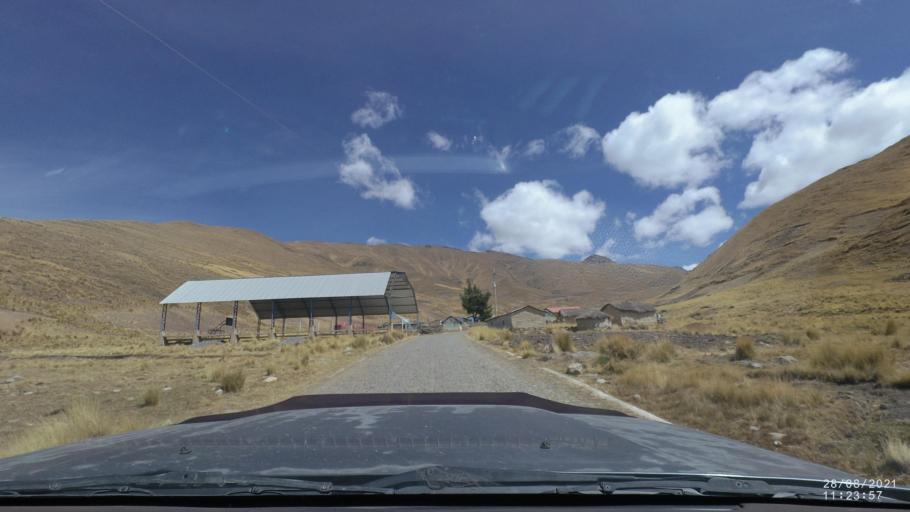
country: BO
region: Cochabamba
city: Sipe Sipe
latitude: -17.1654
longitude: -66.3510
